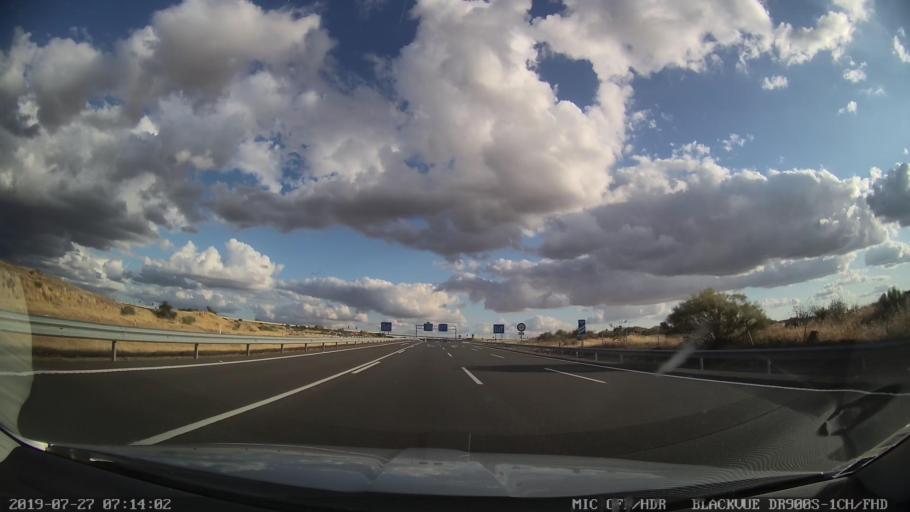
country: ES
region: Extremadura
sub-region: Provincia de Caceres
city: Trujillo
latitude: 39.5003
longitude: -5.8403
